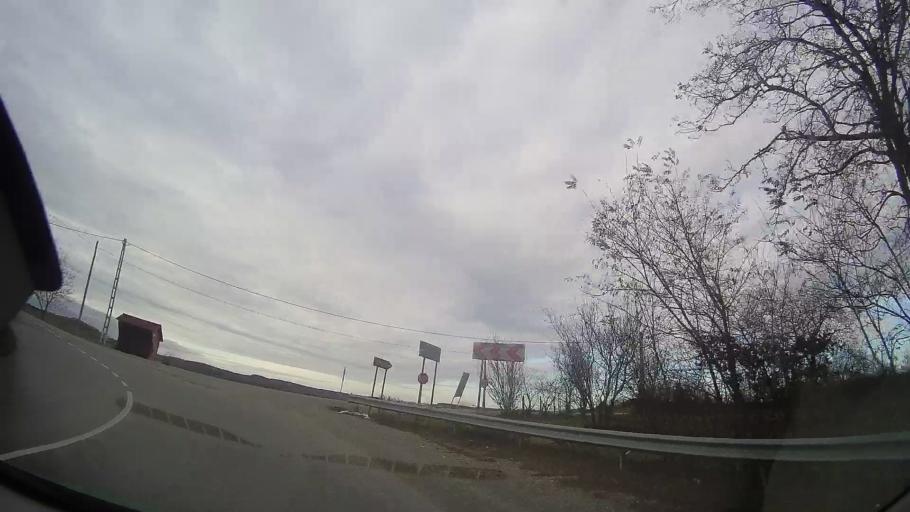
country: RO
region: Bistrita-Nasaud
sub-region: Comuna Budesti
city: Budesti
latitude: 46.8930
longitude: 24.2451
